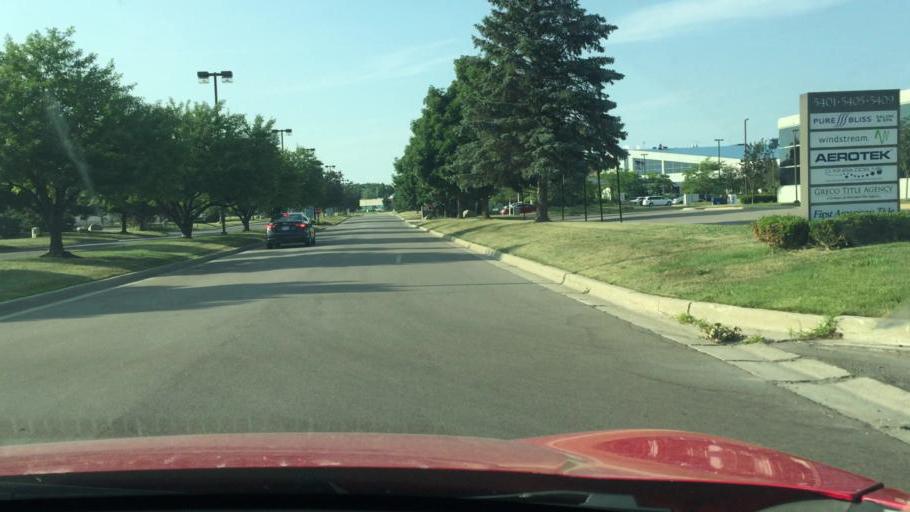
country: US
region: Michigan
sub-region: Genesee County
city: Flint
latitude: 42.9452
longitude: -83.7209
